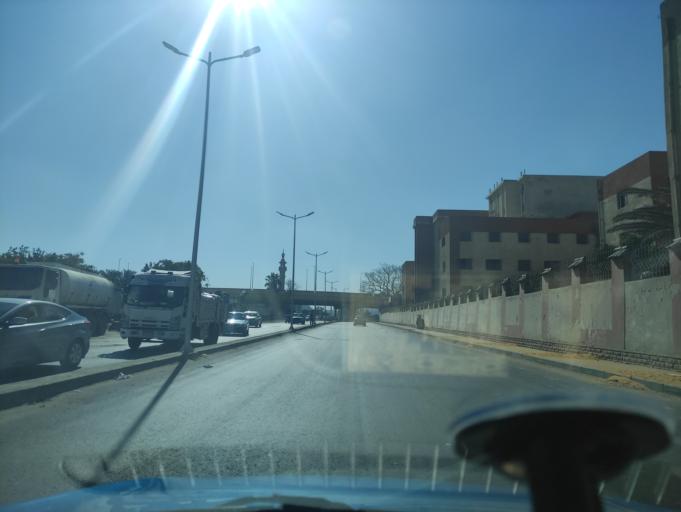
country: EG
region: Muhafazat al Qahirah
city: Cairo
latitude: 30.0569
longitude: 31.2785
